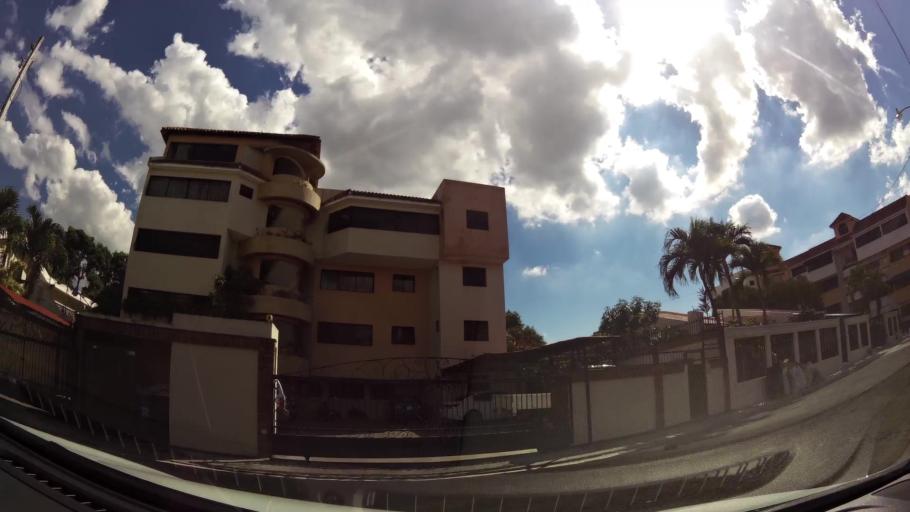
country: DO
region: Santiago
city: Santiago de los Caballeros
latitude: 19.4533
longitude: -70.6695
